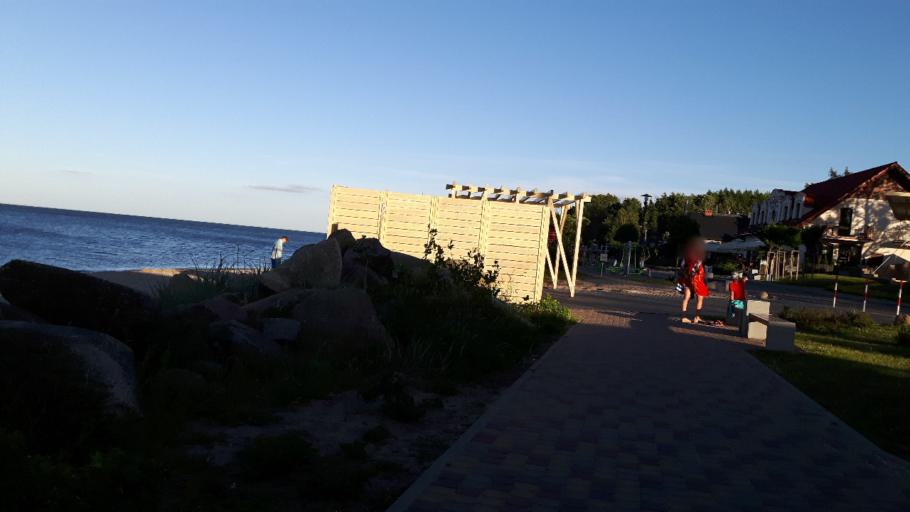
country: PL
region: Pomeranian Voivodeship
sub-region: Powiat pucki
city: Mosty
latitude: 54.6092
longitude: 18.5140
